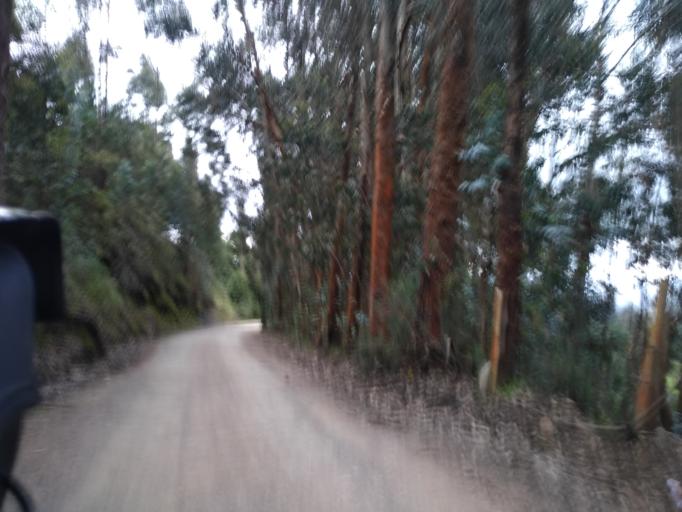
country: CO
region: Boyaca
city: Sotaquira
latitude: 5.7569
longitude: -73.2897
